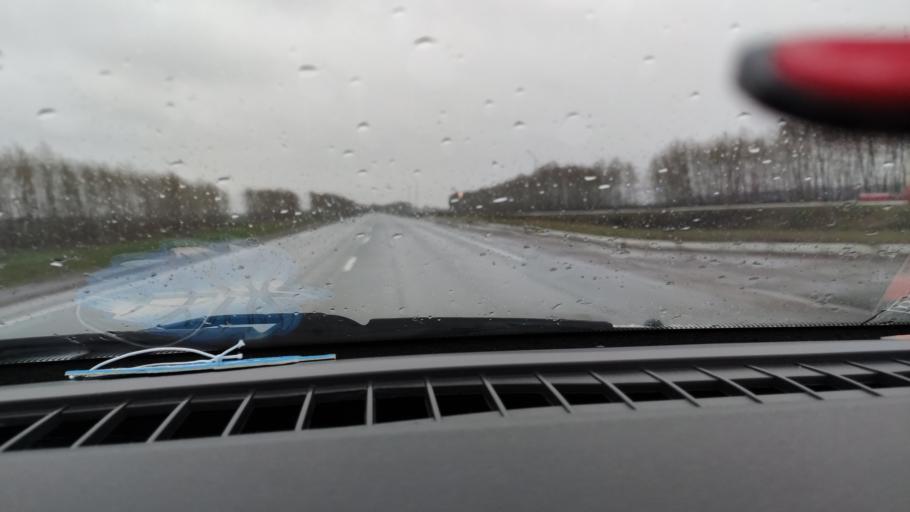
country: RU
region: Tatarstan
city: Mendeleyevsk
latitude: 55.9151
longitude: 52.2722
